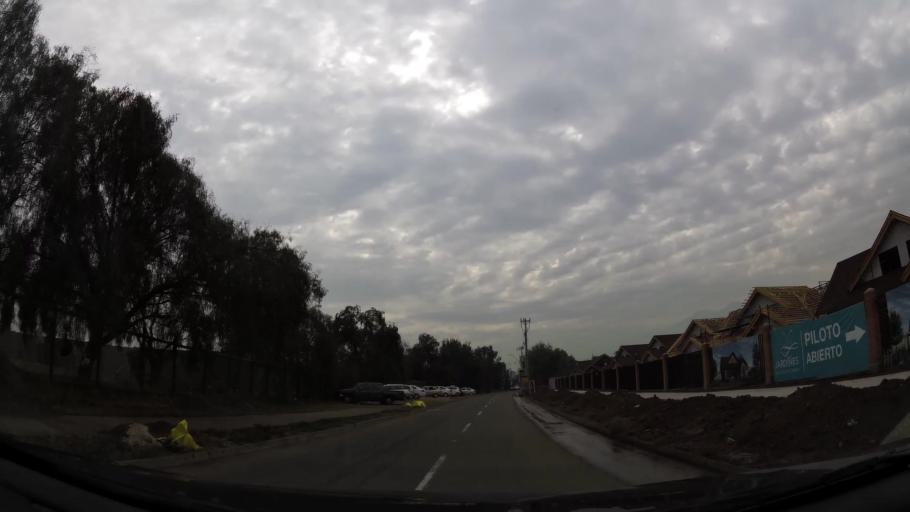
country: CL
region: Santiago Metropolitan
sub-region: Provincia de Chacabuco
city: Chicureo Abajo
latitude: -33.2165
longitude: -70.6635
